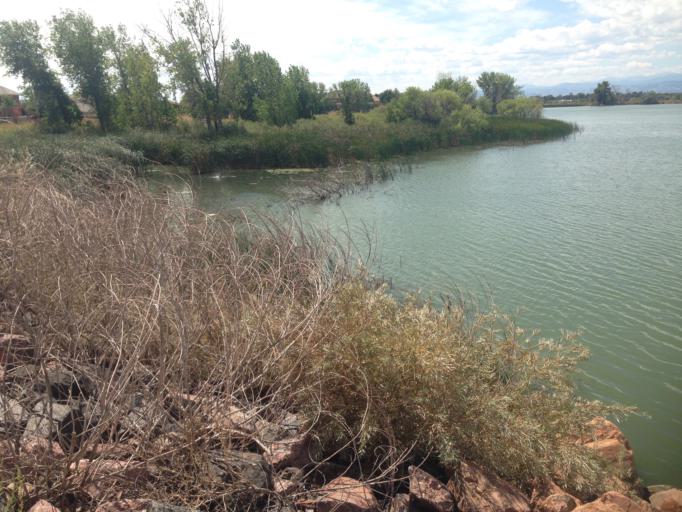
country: US
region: Colorado
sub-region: Adams County
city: Northglenn
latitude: 39.9546
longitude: -105.0075
